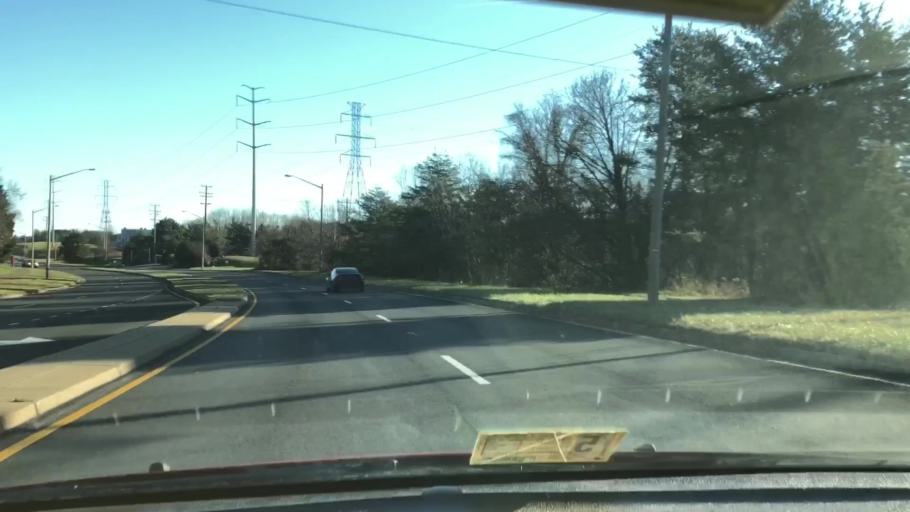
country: US
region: Virginia
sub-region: Fairfax County
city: Franconia
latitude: 38.7638
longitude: -77.1502
